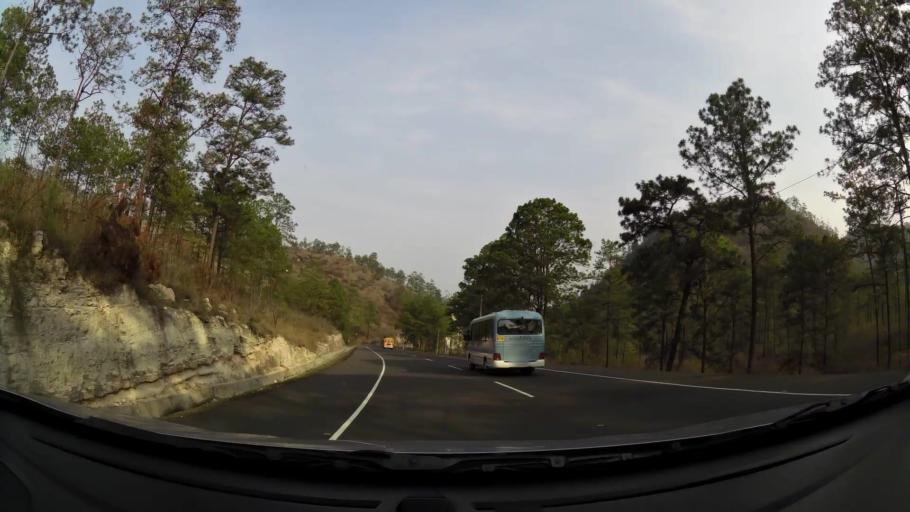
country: HN
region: Francisco Morazan
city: Zambrano
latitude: 14.2878
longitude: -87.4751
